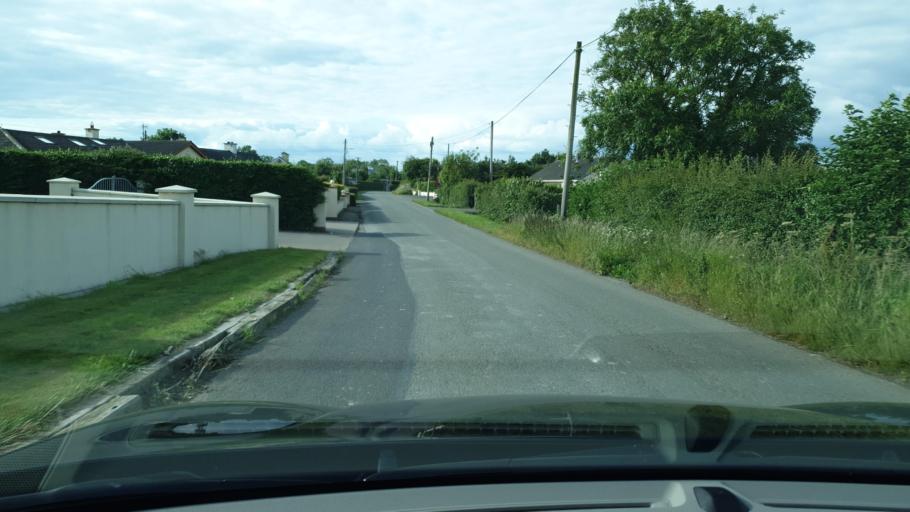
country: IE
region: Leinster
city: Balrothery
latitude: 53.5638
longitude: -6.1654
